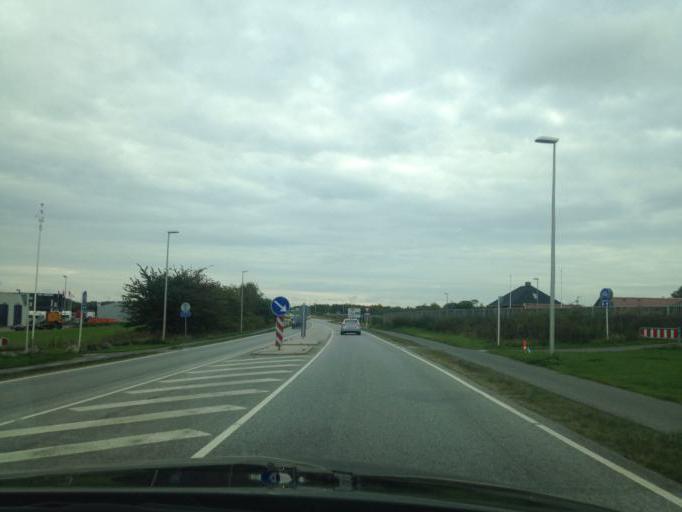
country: DK
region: South Denmark
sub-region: Haderslev Kommune
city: Vojens
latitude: 55.2460
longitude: 9.3933
